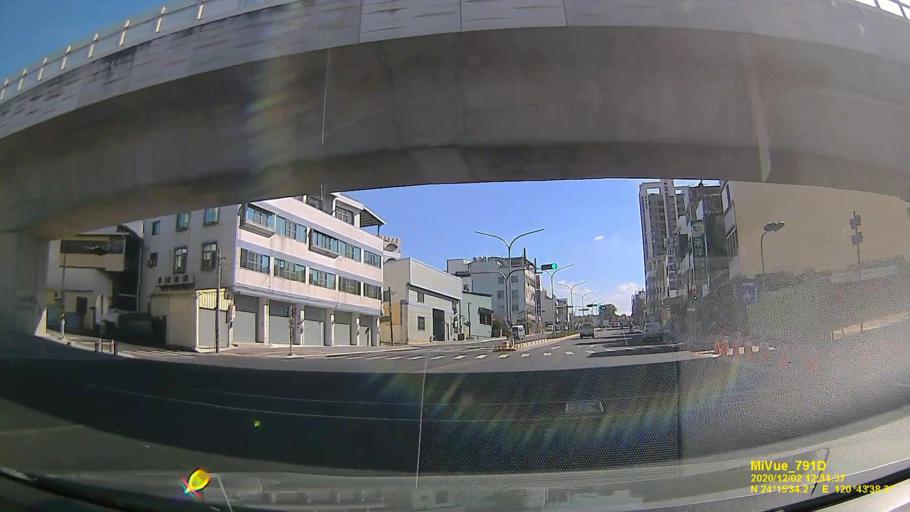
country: TW
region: Taiwan
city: Fengyuan
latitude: 24.2595
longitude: 120.7273
